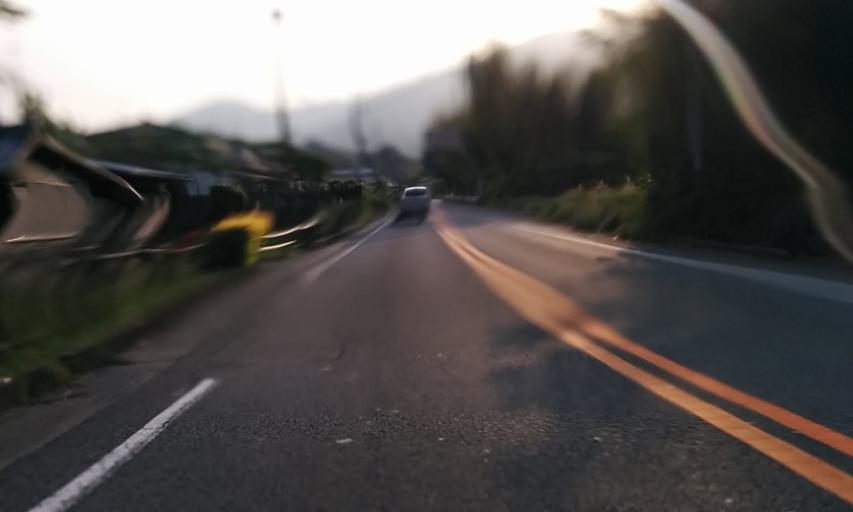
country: JP
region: Ehime
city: Saijo
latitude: 33.8565
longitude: 133.0167
